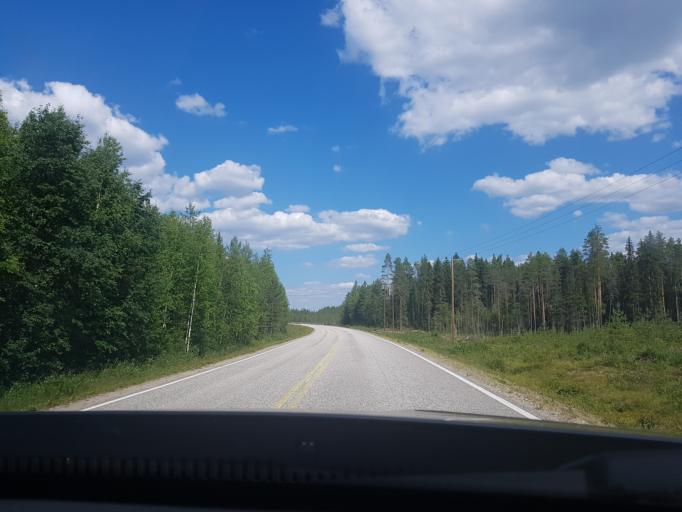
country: FI
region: Kainuu
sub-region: Kehys-Kainuu
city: Kuhmo
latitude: 64.2201
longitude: 29.7960
